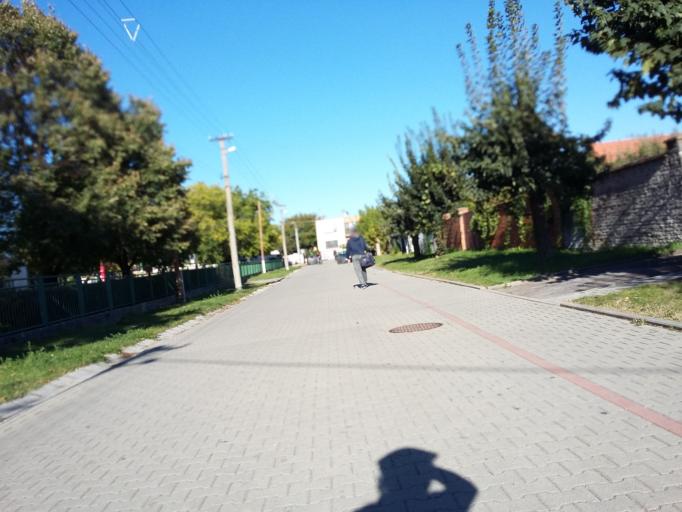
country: SK
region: Bratislavsky
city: Stupava
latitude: 48.3198
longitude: 16.9845
